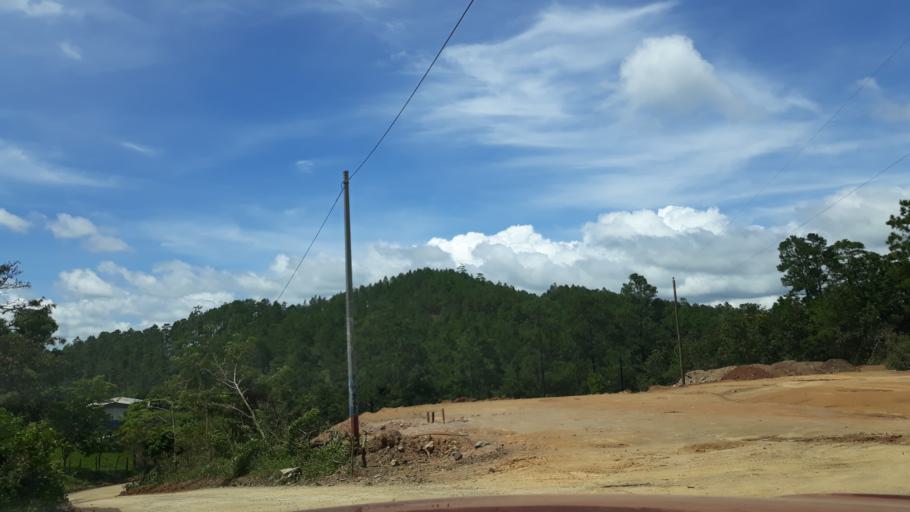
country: HN
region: El Paraiso
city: Santa Cruz
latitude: 13.7543
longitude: -86.6602
